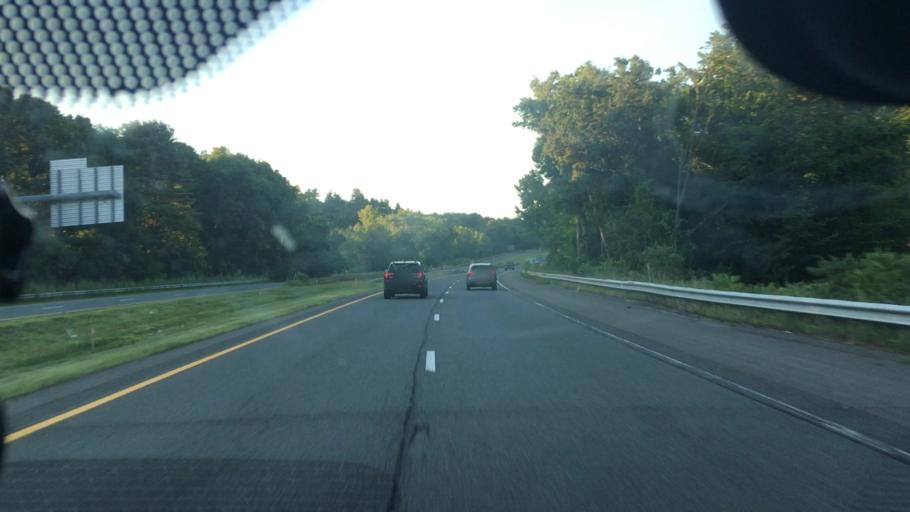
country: US
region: Massachusetts
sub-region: Franklin County
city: Greenfield
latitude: 42.6006
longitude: -72.6159
